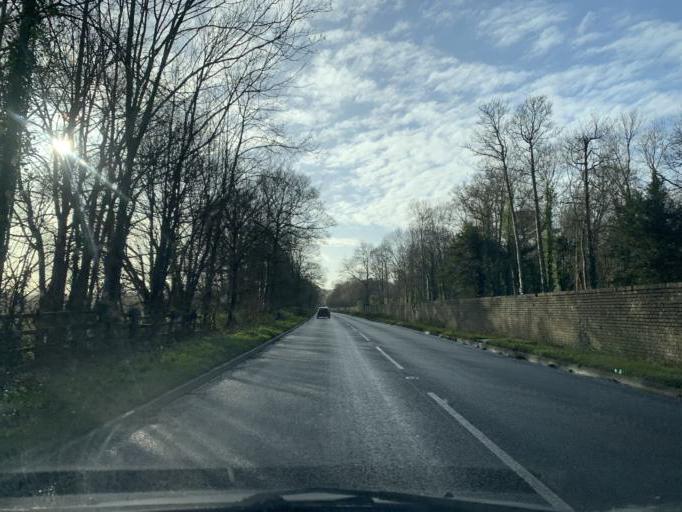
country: GB
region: England
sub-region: Wiltshire
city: Wilton
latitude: 51.0750
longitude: -1.8502
